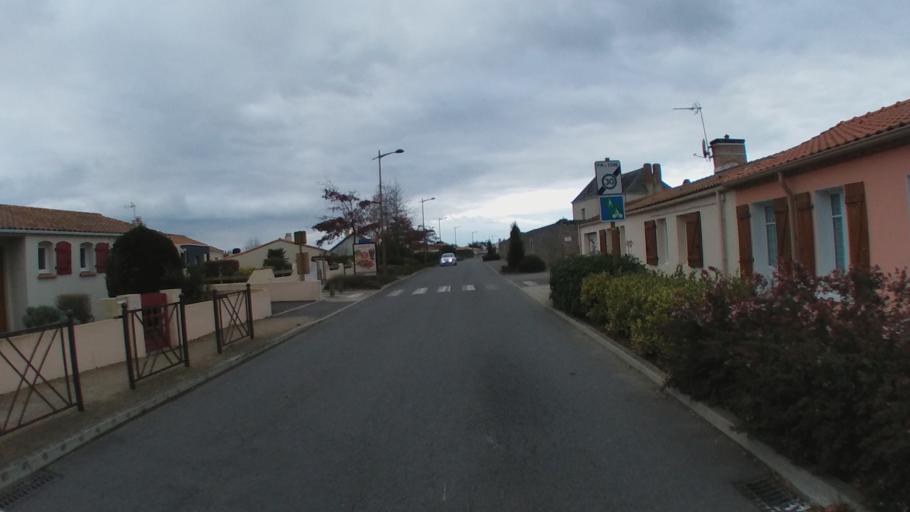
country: FR
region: Pays de la Loire
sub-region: Departement de la Loire-Atlantique
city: Corsept
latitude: 47.2763
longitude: -2.0601
